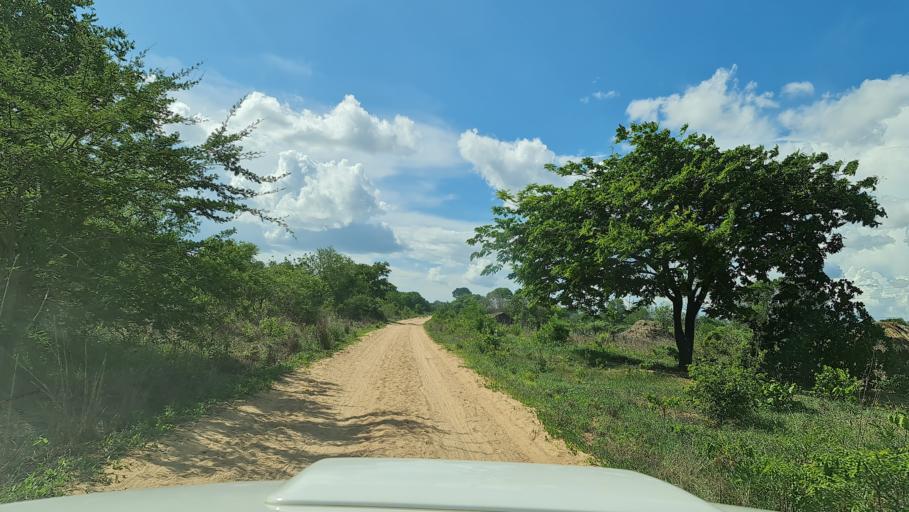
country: MZ
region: Nampula
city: Ilha de Mocambique
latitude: -15.4410
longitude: 40.2862
